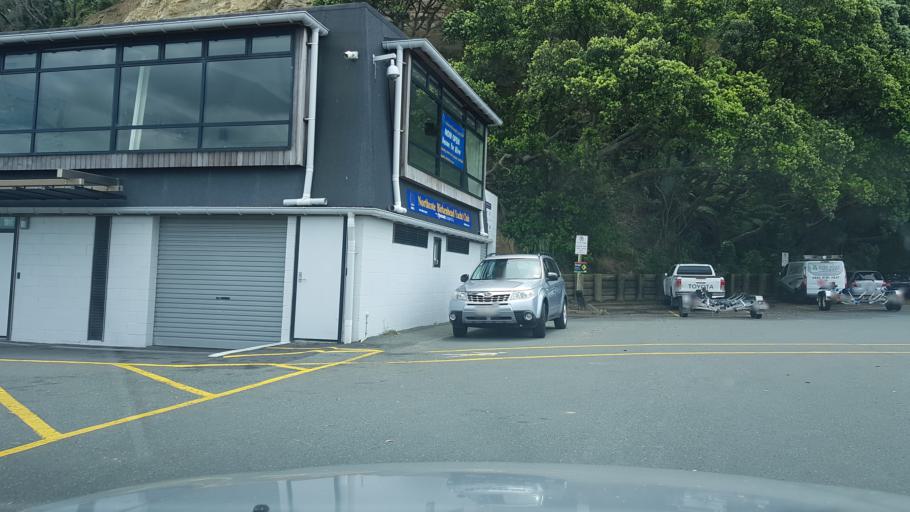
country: NZ
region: Auckland
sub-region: Auckland
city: North Shore
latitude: -36.8229
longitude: 174.7334
